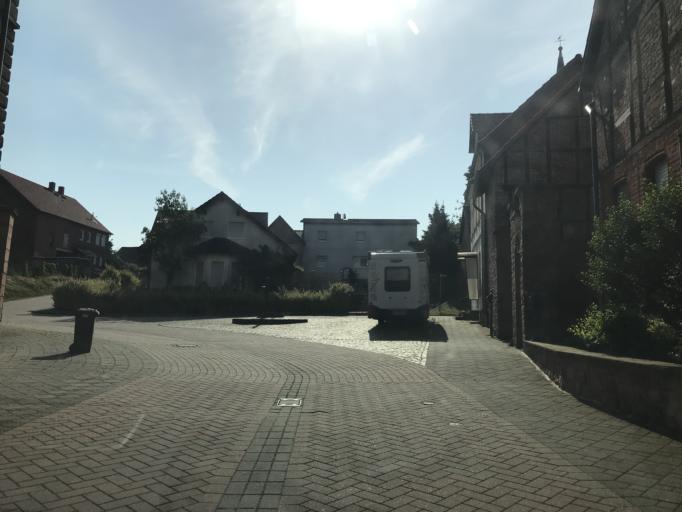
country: DE
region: Saxony-Anhalt
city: Altenhausen
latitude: 52.2540
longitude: 11.2233
